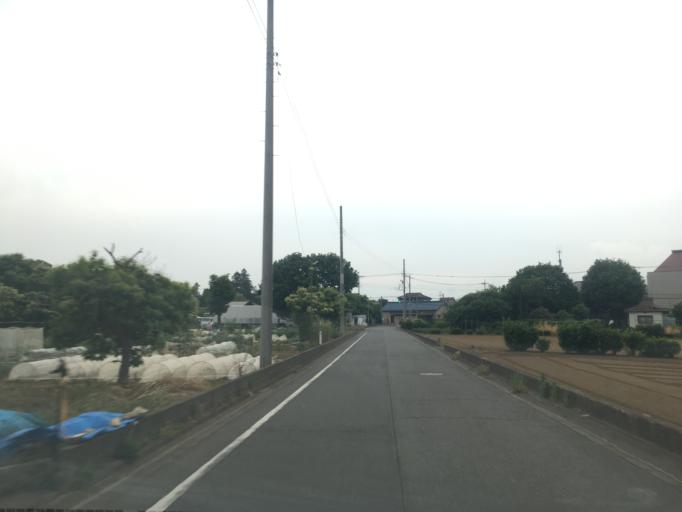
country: JP
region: Saitama
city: Tokorozawa
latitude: 35.8224
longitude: 139.4500
